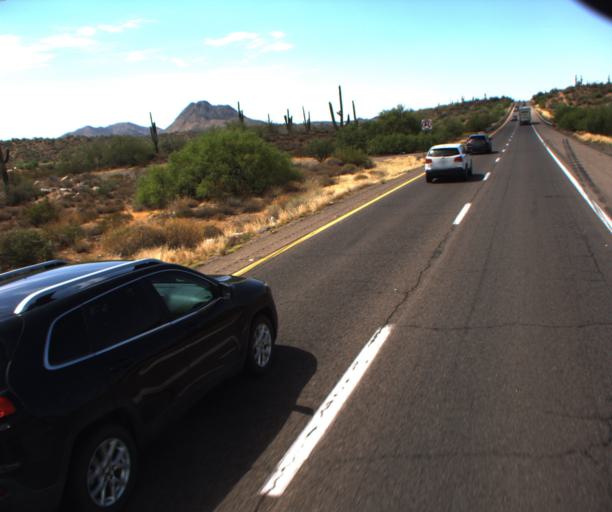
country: US
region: Arizona
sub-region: Maricopa County
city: New River
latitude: 33.9425
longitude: -112.1410
